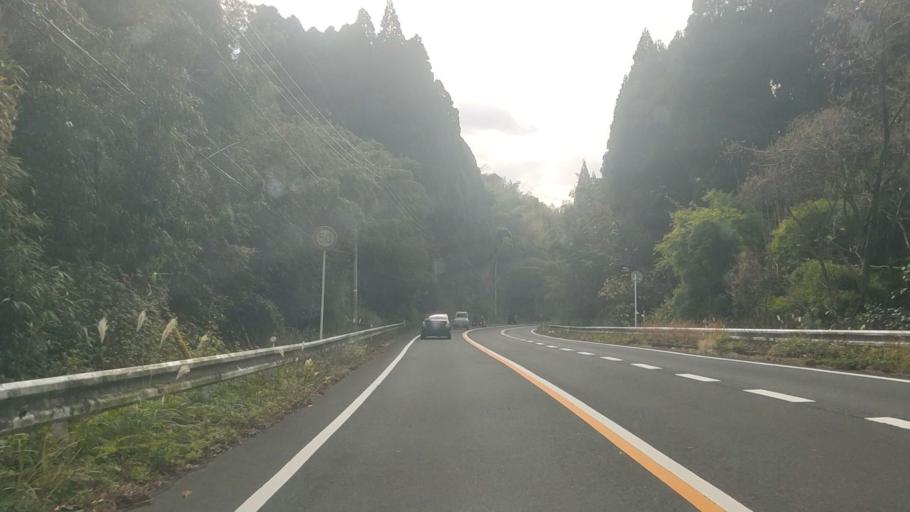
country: JP
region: Kagoshima
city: Kajiki
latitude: 31.7629
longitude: 130.6811
